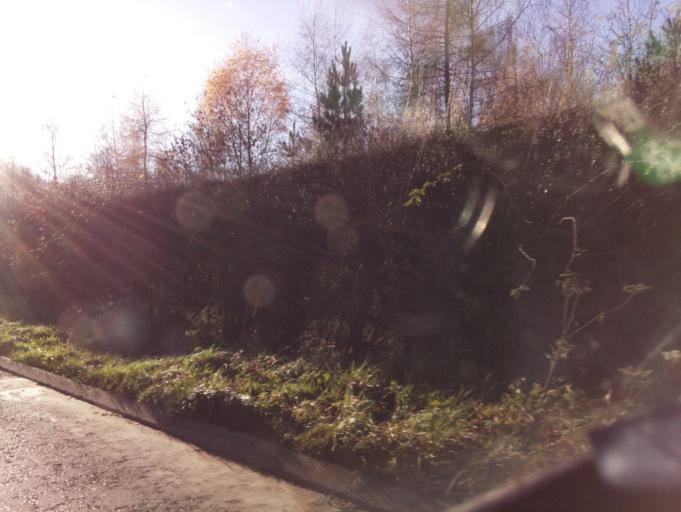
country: GB
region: England
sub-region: Staffordshire
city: Barton under Needwood
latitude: 52.8109
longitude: -1.7364
